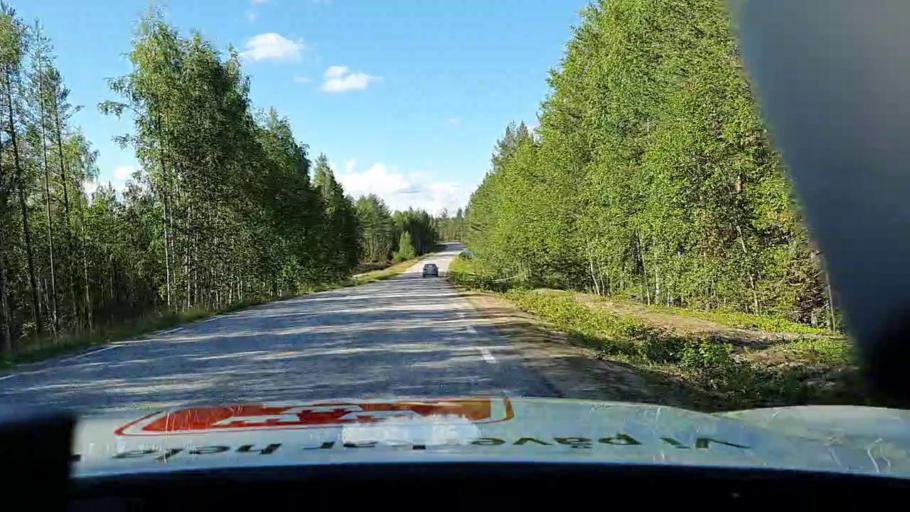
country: SE
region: Norrbotten
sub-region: Overkalix Kommun
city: OEverkalix
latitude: 66.2426
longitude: 22.9248
